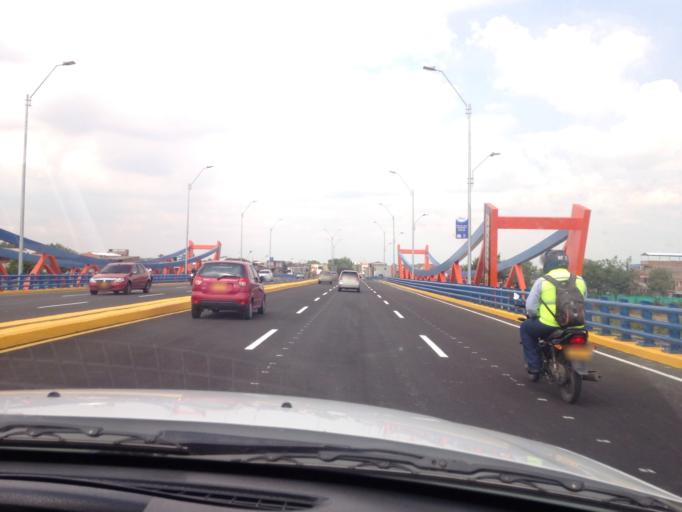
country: CO
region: Valle del Cauca
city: Cali
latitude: 3.3931
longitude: -76.5138
